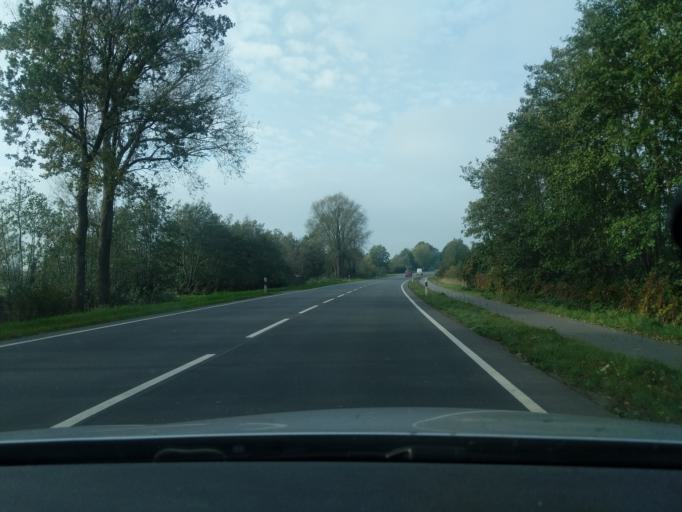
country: DE
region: Lower Saxony
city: Neuhaus an der Oste
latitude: 53.7984
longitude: 9.0403
